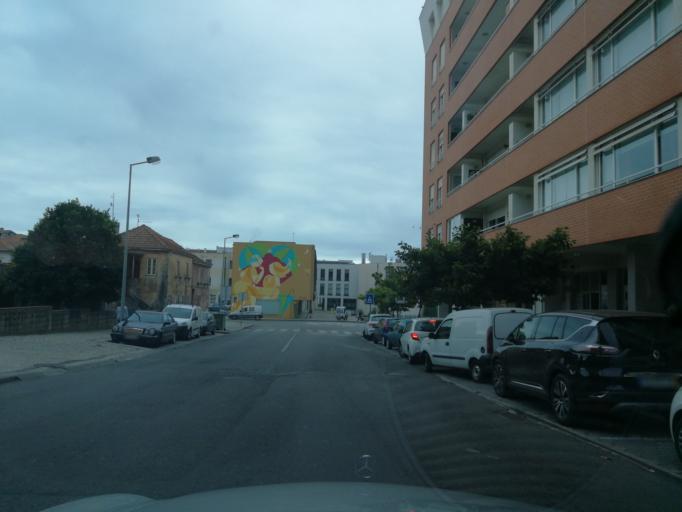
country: PT
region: Aveiro
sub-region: Agueda
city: Agueda
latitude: 40.5769
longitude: -8.4470
